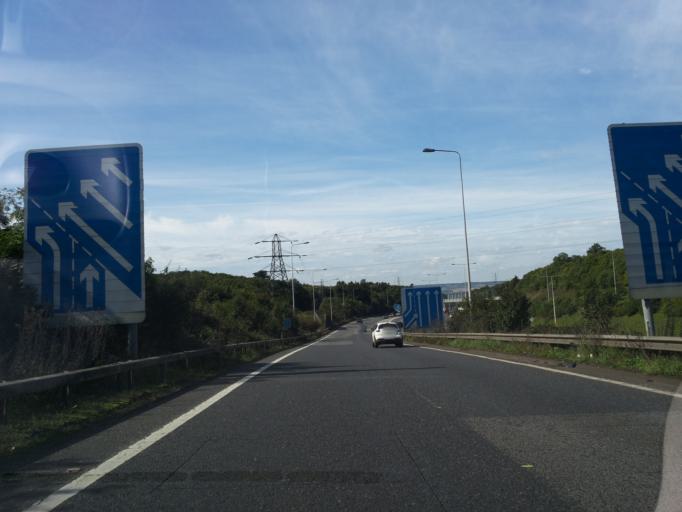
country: GB
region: England
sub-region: Kent
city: Boxley
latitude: 51.2875
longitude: 0.5493
